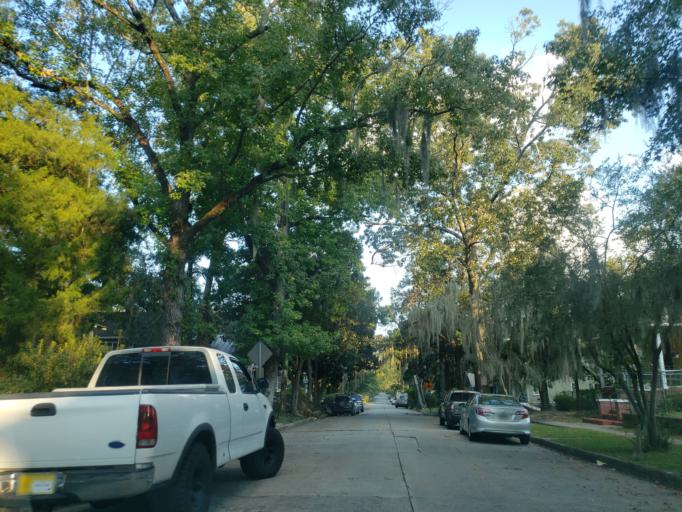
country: US
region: Georgia
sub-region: Chatham County
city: Savannah
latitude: 32.0552
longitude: -81.0802
